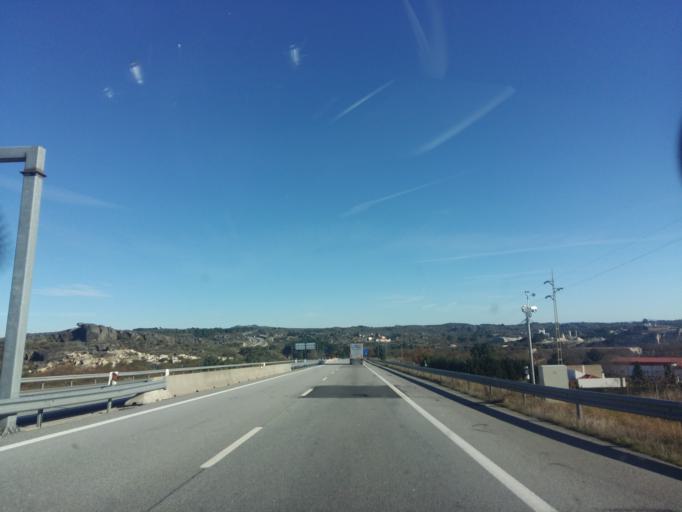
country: PT
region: Guarda
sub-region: Guarda
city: Sequeira
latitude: 40.5735
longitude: -7.2001
